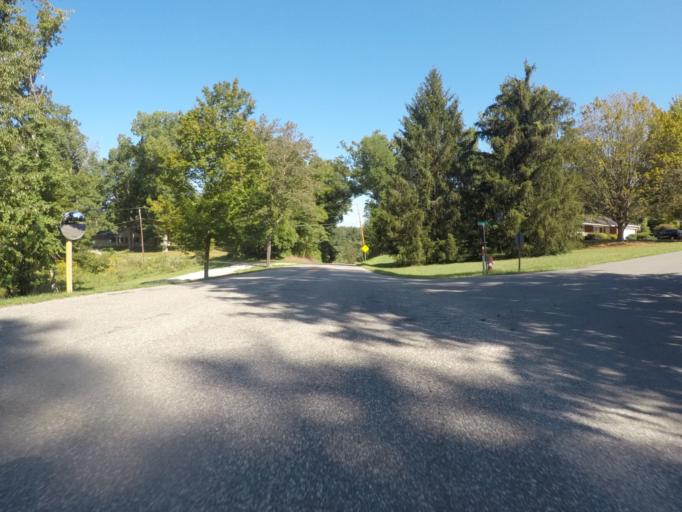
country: US
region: Kentucky
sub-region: Greenup County
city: Russell
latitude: 38.4962
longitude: -82.6959
